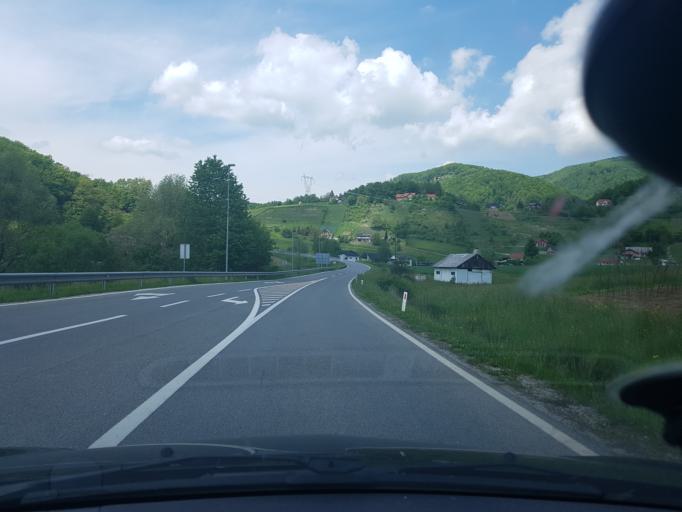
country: SI
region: Rogaska Slatina
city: Rogaska Slatina
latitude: 46.2494
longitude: 15.6391
